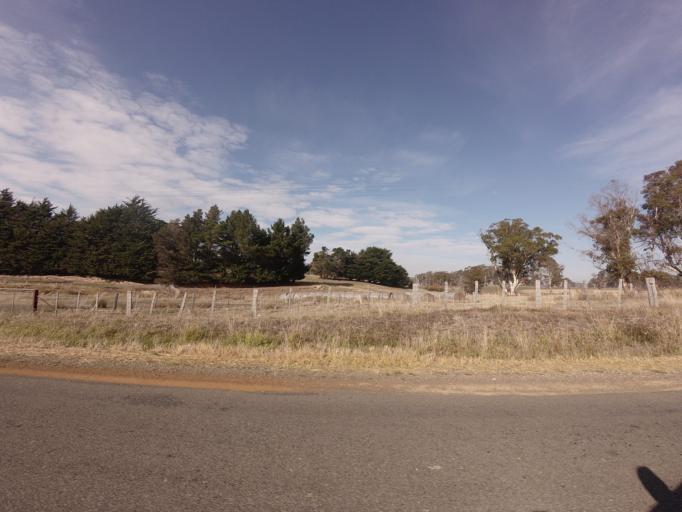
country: AU
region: Tasmania
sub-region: Sorell
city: Sorell
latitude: -42.4454
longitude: 147.4670
